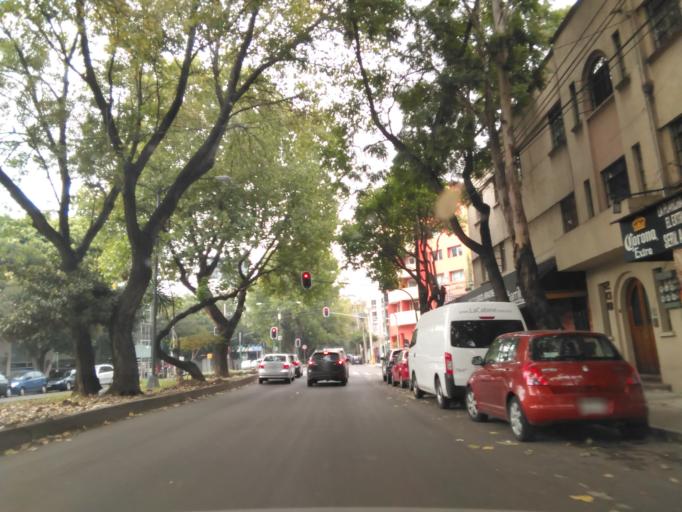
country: MX
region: Mexico City
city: Colonia del Valle
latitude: 19.3950
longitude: -99.1681
